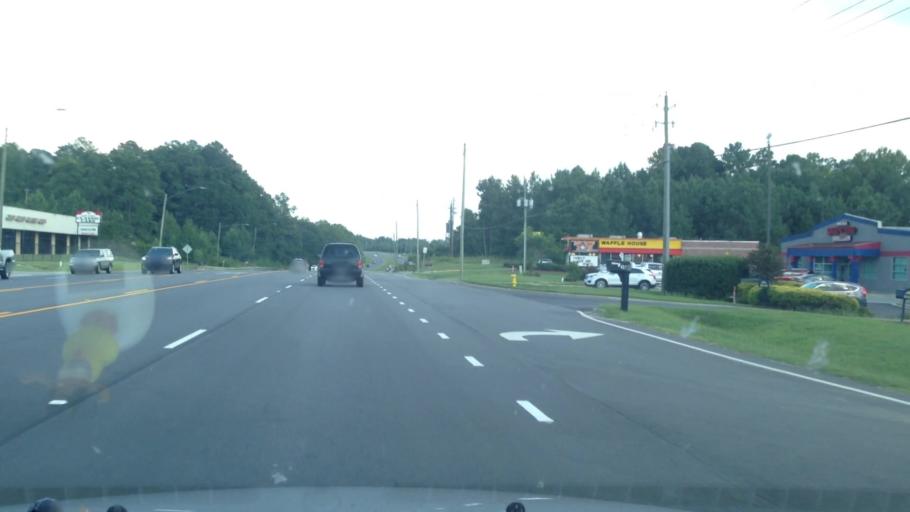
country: US
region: North Carolina
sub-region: Harnett County
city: Lillington
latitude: 35.4159
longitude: -78.7995
